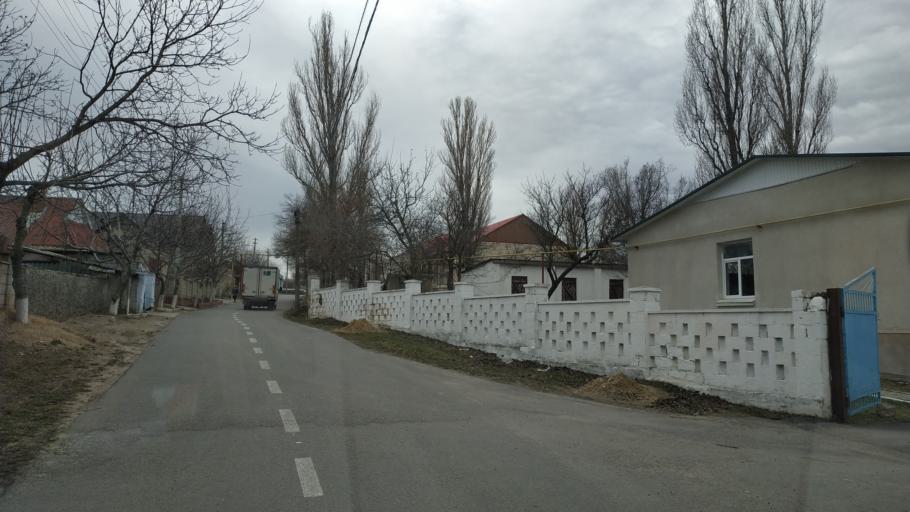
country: MD
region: Telenesti
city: Cocieri
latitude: 47.3482
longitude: 29.0908
